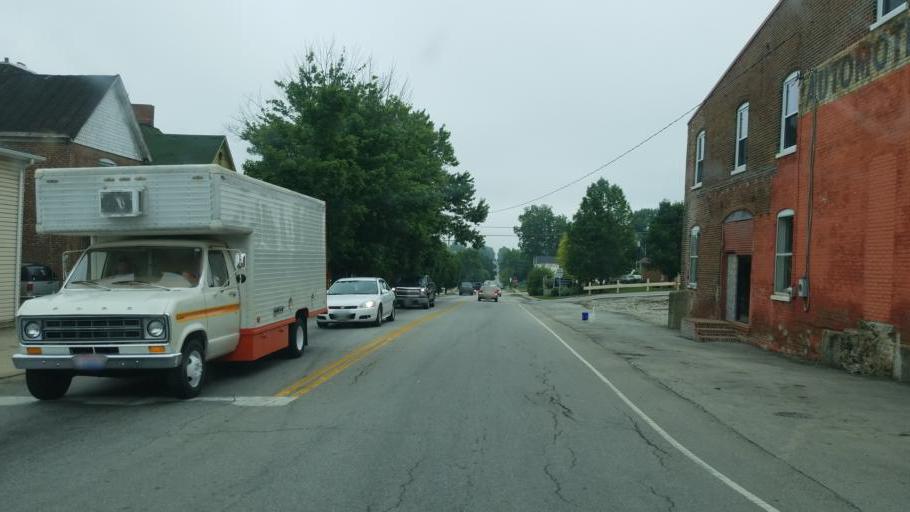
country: US
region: Ohio
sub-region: Highland County
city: Hillsboro
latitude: 39.2027
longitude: -83.6140
